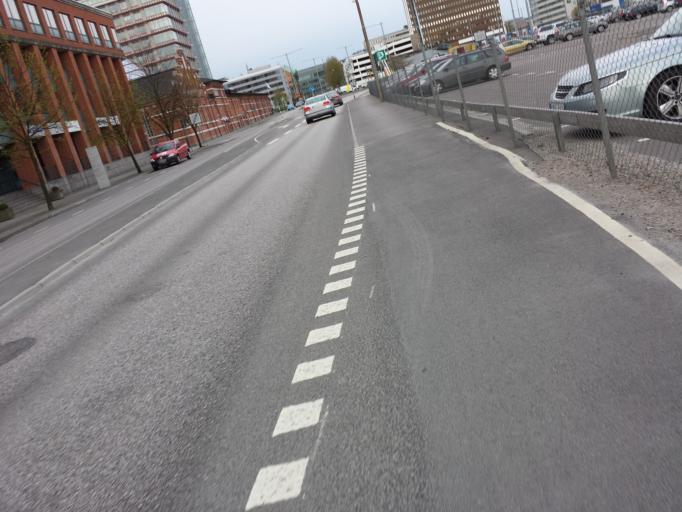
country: SE
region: Skane
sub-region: Malmo
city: Malmoe
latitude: 55.6120
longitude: 13.0047
